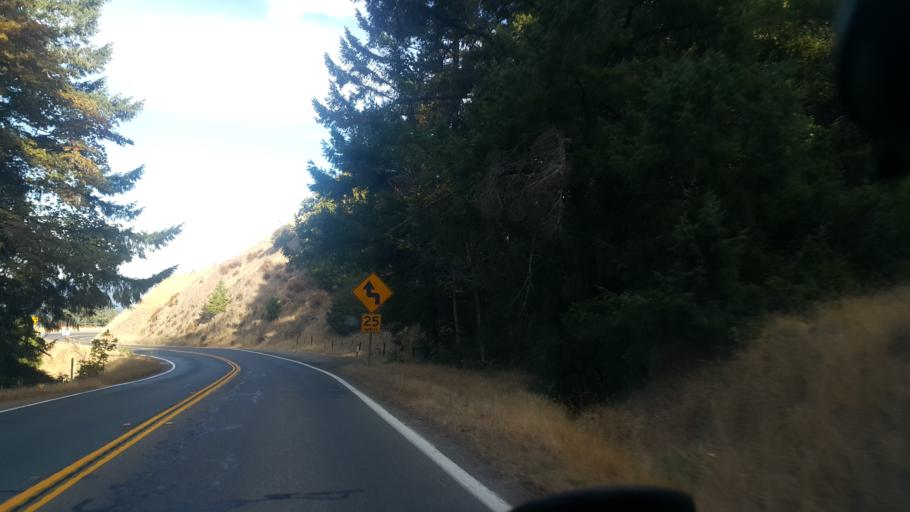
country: US
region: California
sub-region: Mendocino County
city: Brooktrails
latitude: 39.3902
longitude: -123.4444
